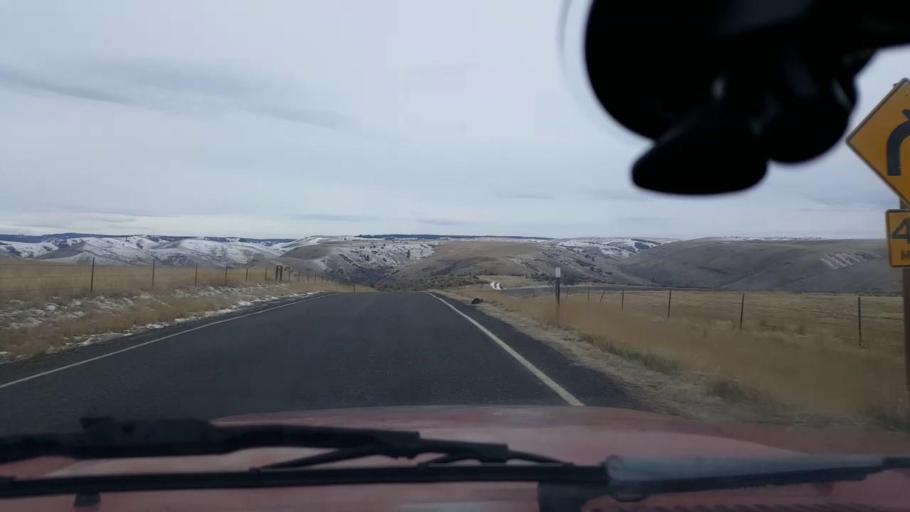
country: US
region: Washington
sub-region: Asotin County
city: Clarkston Heights-Vineland
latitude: 46.3126
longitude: -117.3384
